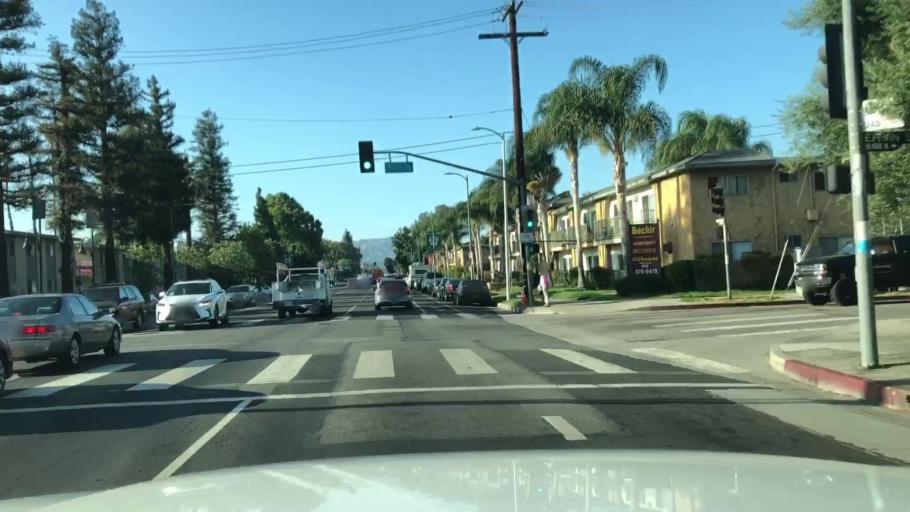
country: US
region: California
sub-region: Los Angeles County
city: Northridge
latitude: 34.1837
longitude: -118.5360
